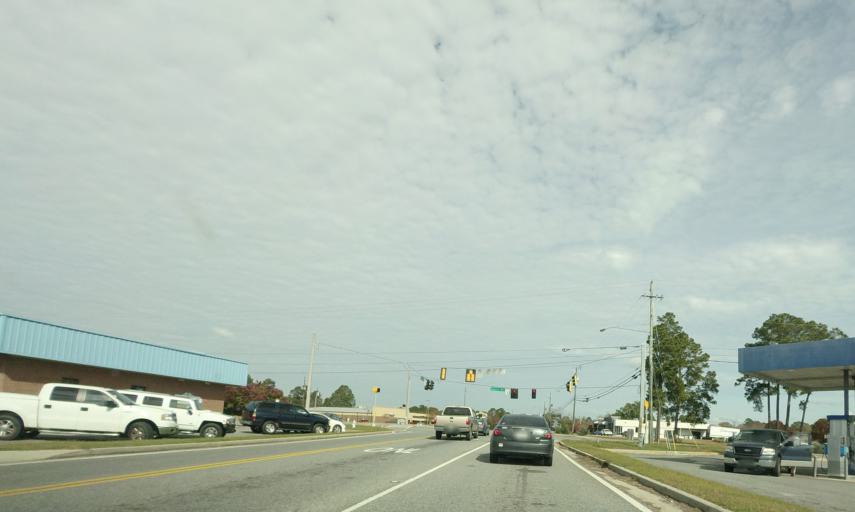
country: US
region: Georgia
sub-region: Laurens County
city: Dublin
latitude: 32.5277
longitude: -82.9433
